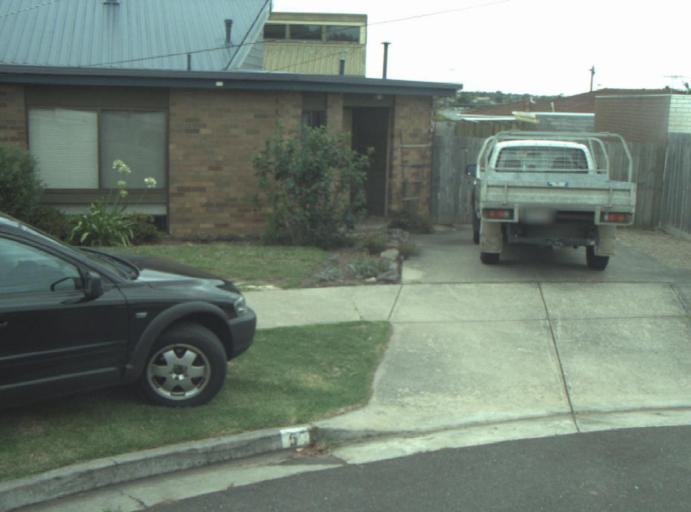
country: AU
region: Victoria
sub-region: Greater Geelong
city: Wandana Heights
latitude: -38.2004
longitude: 144.3305
